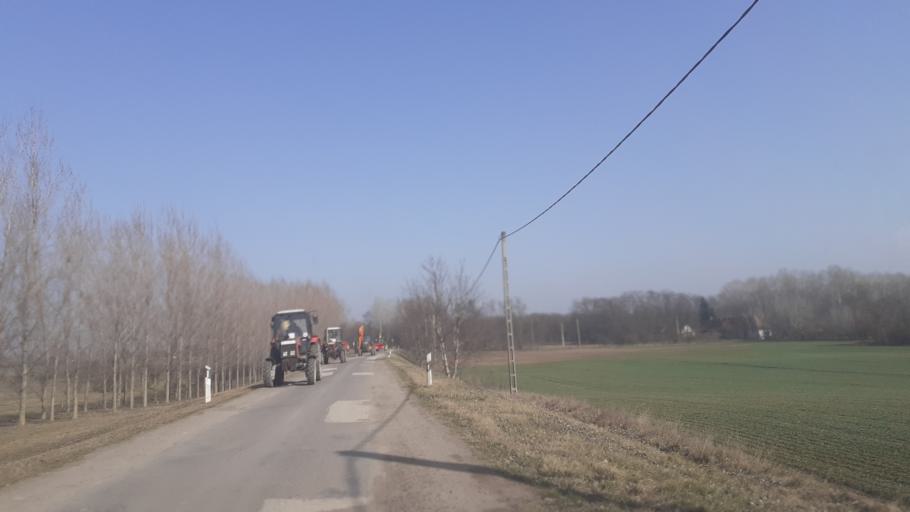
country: HU
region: Pest
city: Domsod
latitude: 47.0702
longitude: 18.9999
